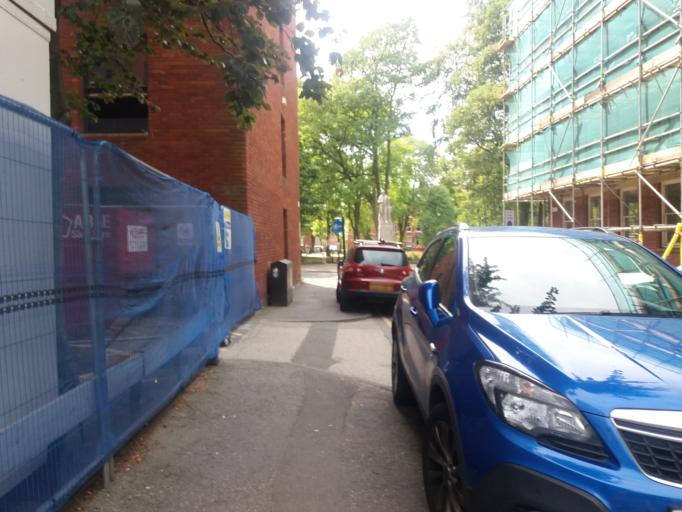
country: GB
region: England
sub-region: Lancashire
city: Preston
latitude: 53.7562
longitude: -2.7003
